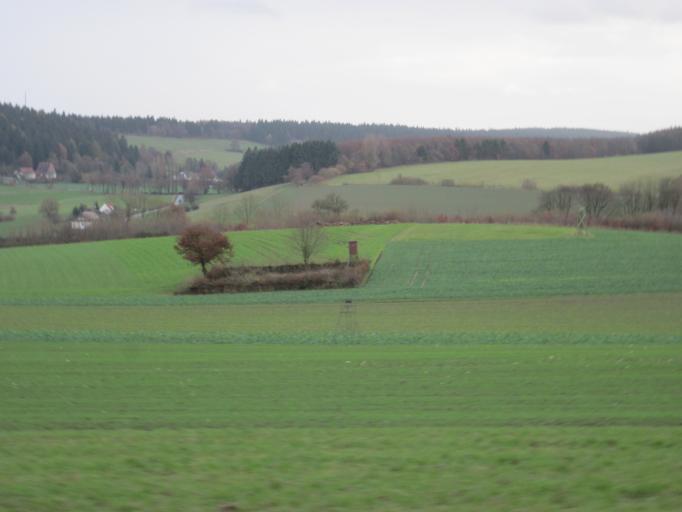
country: DE
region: North Rhine-Westphalia
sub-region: Regierungsbezirk Detmold
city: Altenbeken
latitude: 51.8078
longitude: 8.9337
